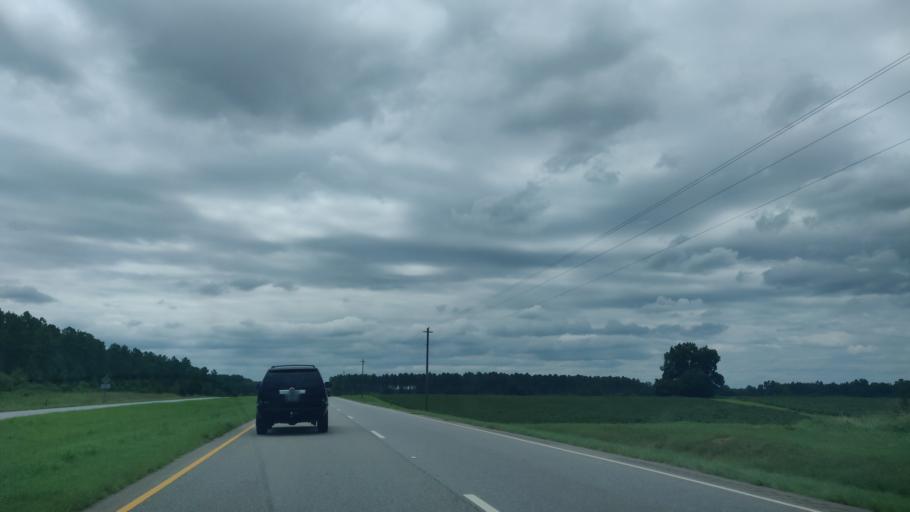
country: US
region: Georgia
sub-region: Terrell County
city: Dawson
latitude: 31.8351
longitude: -84.4668
